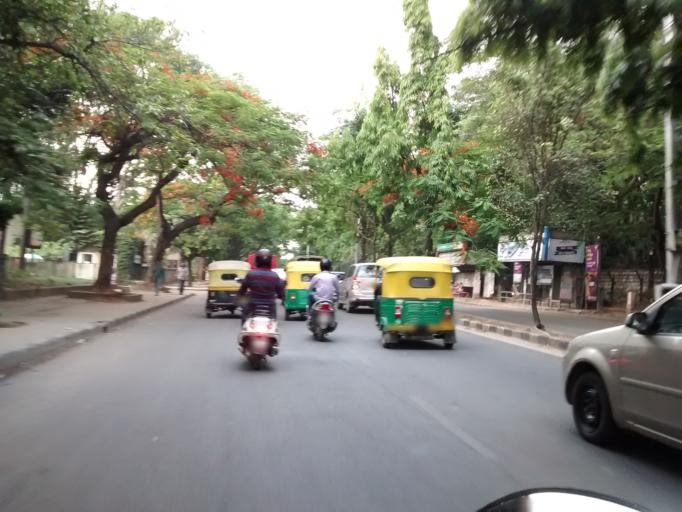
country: IN
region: Karnataka
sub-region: Bangalore Urban
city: Bangalore
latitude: 12.9595
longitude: 77.6512
